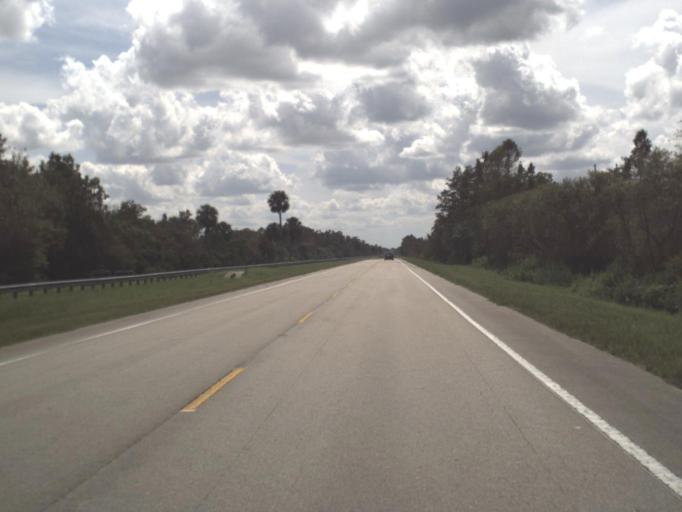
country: US
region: Florida
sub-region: Collier County
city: Orangetree
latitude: 26.0802
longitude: -81.3447
